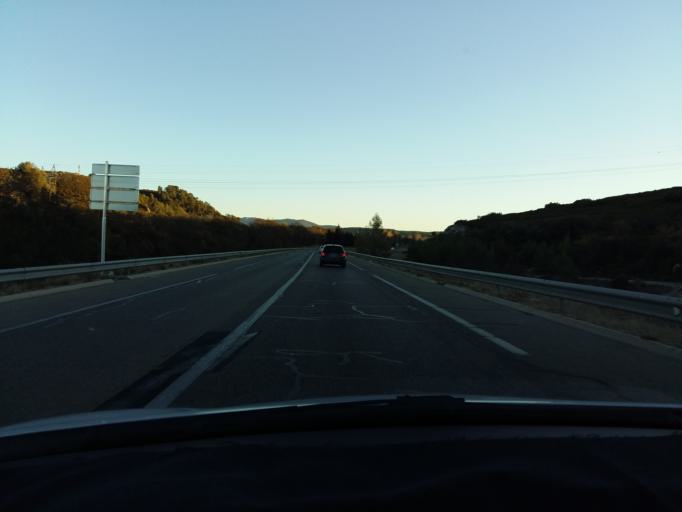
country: FR
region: Provence-Alpes-Cote d'Azur
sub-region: Departement des Bouches-du-Rhone
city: Cabries
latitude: 43.4863
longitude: 5.3528
